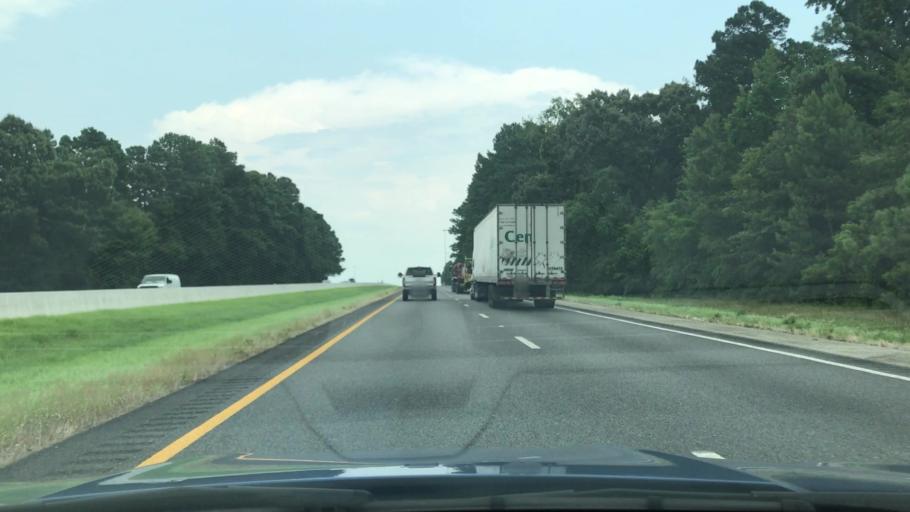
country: US
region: Texas
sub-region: Gregg County
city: Liberty City
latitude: 32.4348
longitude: -94.9548
